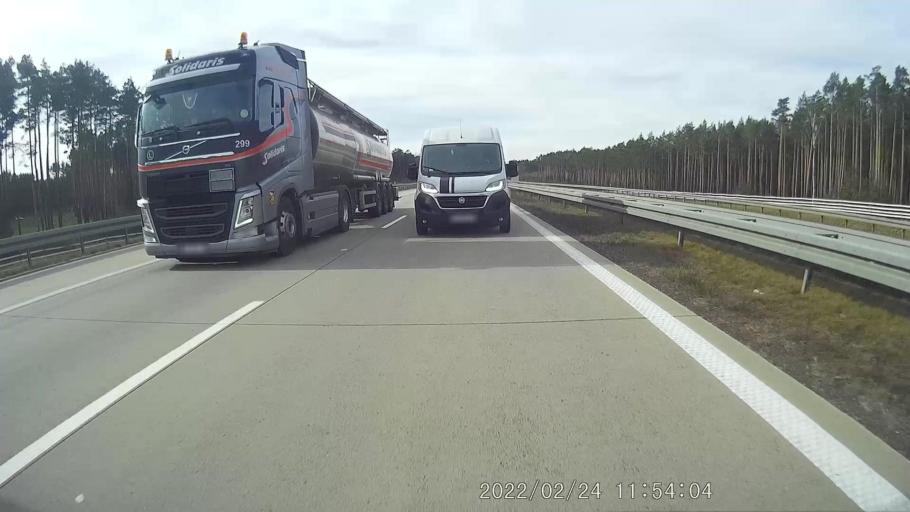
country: PL
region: Lower Silesian Voivodeship
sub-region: Powiat polkowicki
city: Radwanice
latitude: 51.6331
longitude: 15.9842
